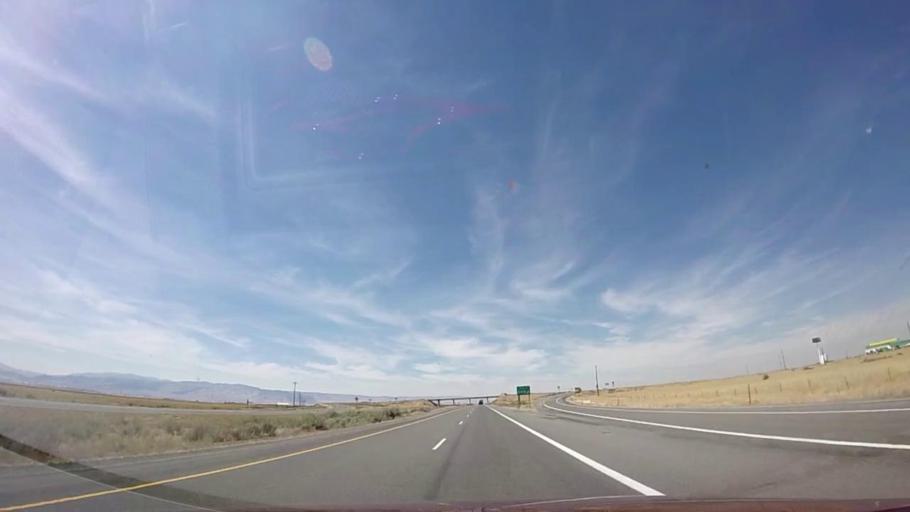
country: US
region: Idaho
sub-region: Minidoka County
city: Rupert
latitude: 42.3253
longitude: -113.2092
